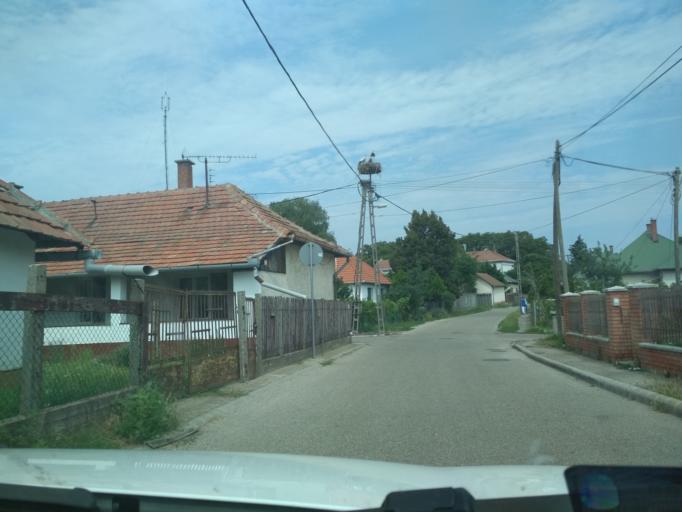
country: HU
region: Jasz-Nagykun-Szolnok
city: Tiszafured
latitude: 47.6191
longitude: 20.7585
